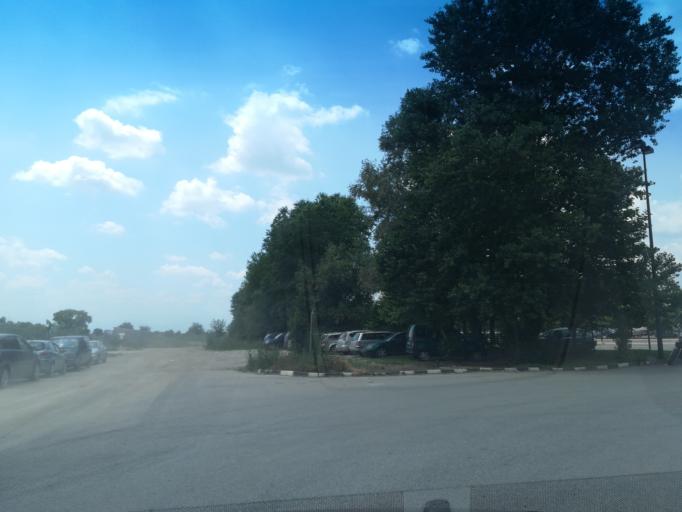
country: BG
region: Plovdiv
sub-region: Obshtina Plovdiv
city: Plovdiv
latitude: 42.1650
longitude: 24.6757
